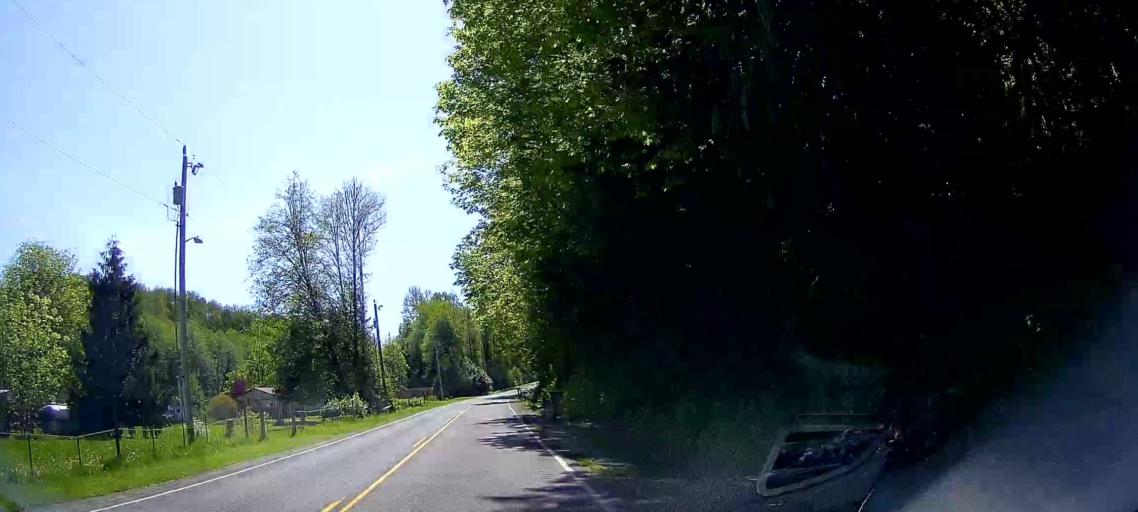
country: US
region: Washington
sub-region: Snohomish County
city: Darrington
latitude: 48.5047
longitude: -121.6642
